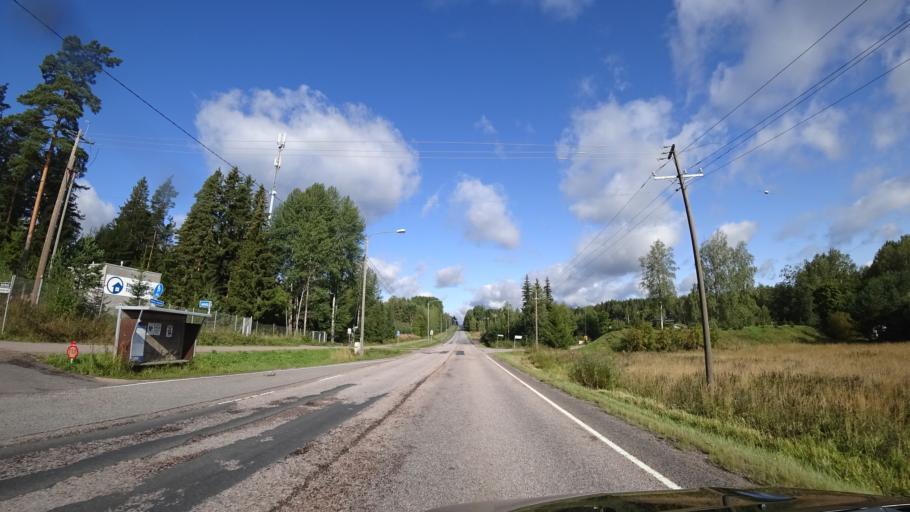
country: FI
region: Uusimaa
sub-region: Helsinki
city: Tuusula
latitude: 60.4337
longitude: 24.9878
